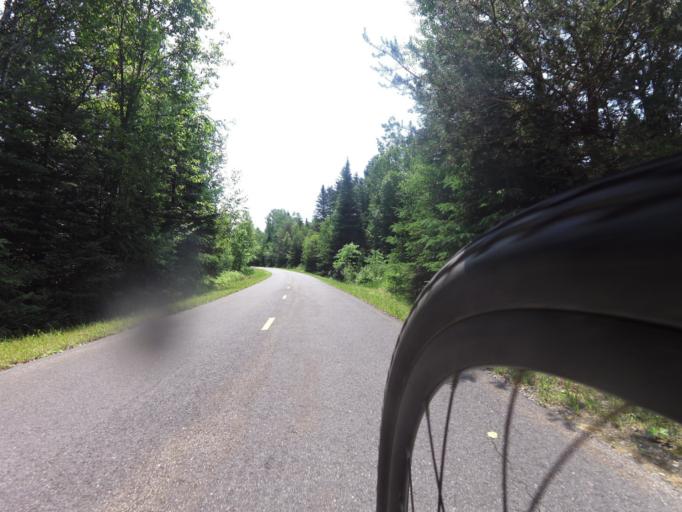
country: CA
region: Quebec
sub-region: Laurentides
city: Mont-Tremblant
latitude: 46.1361
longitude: -74.5969
